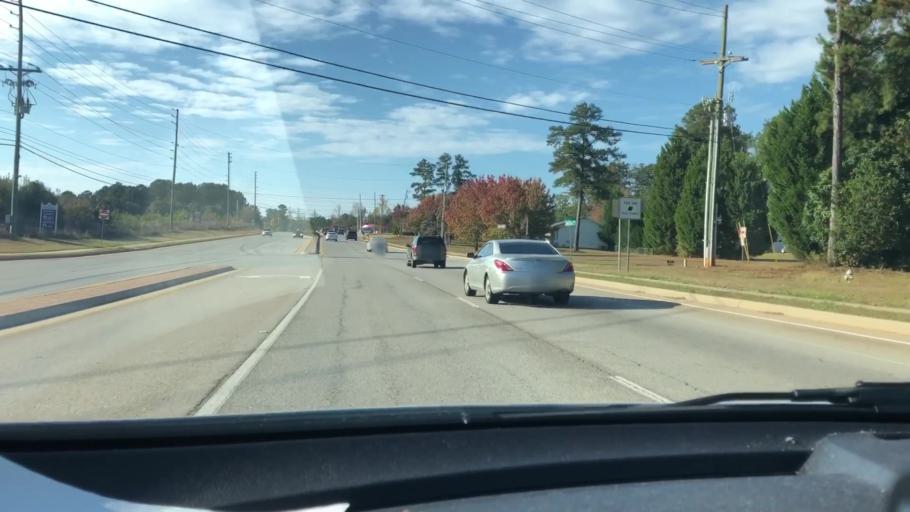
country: US
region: Georgia
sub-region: Henry County
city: McDonough
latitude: 33.4558
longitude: -84.1703
